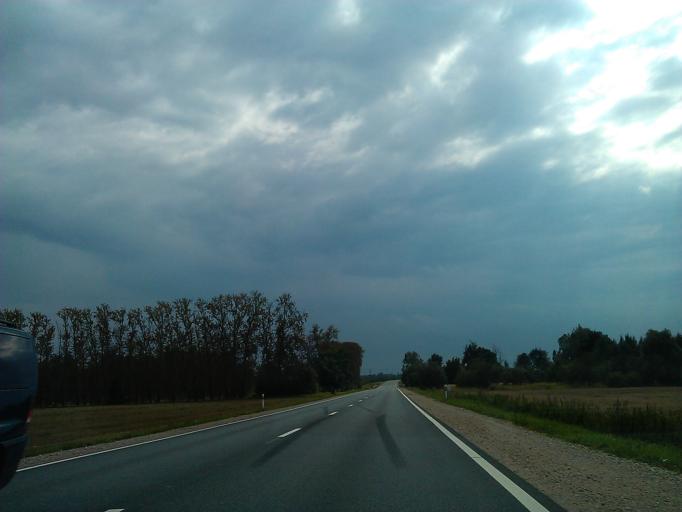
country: LV
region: Lecava
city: Iecava
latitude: 56.5471
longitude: 24.1733
